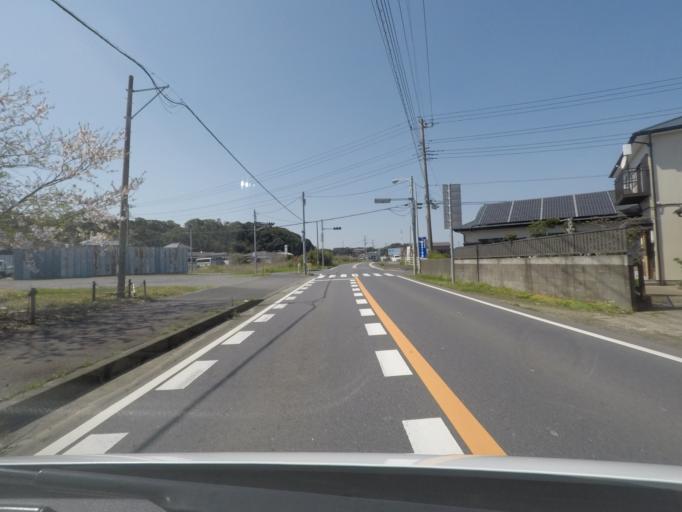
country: JP
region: Chiba
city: Asahi
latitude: 35.8031
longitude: 140.7136
